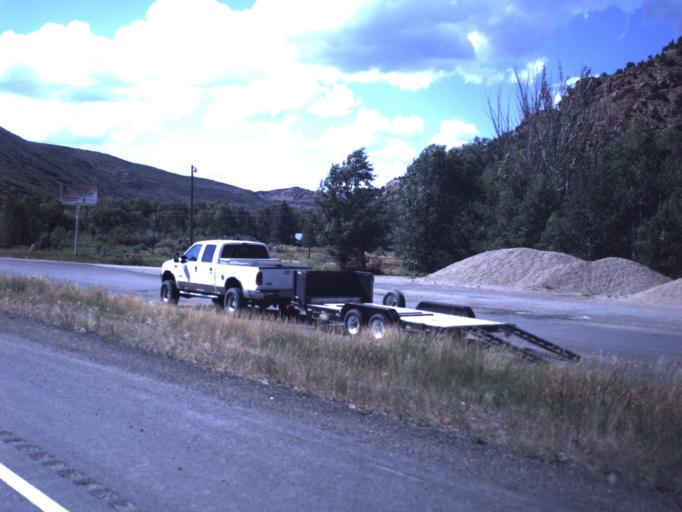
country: US
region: Utah
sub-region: Duchesne County
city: Duchesne
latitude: 40.2003
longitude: -110.9058
